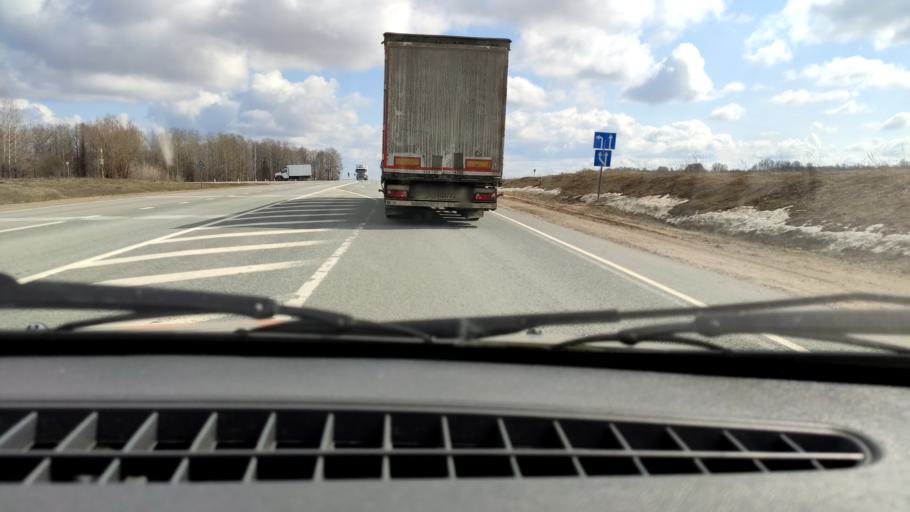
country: RU
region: Bashkortostan
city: Kudeyevskiy
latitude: 54.8171
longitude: 56.7914
